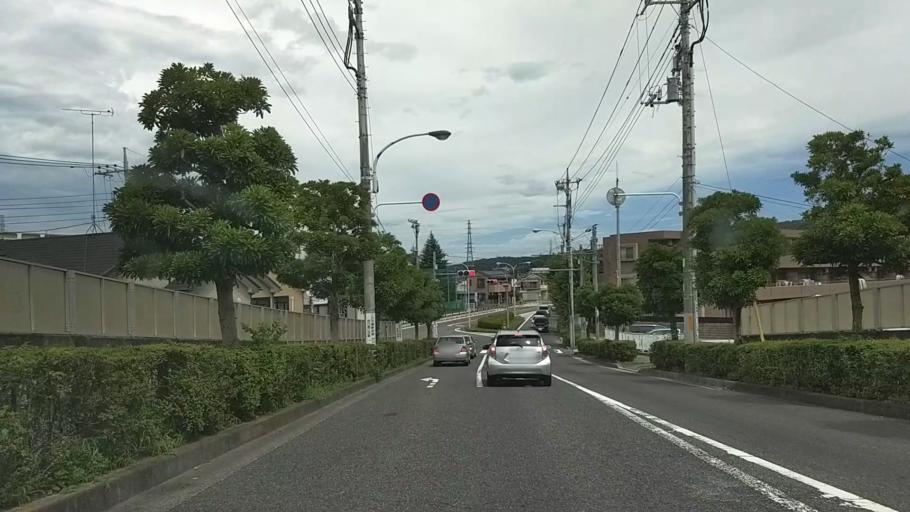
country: JP
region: Tokyo
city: Hachioji
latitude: 35.6415
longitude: 139.3650
